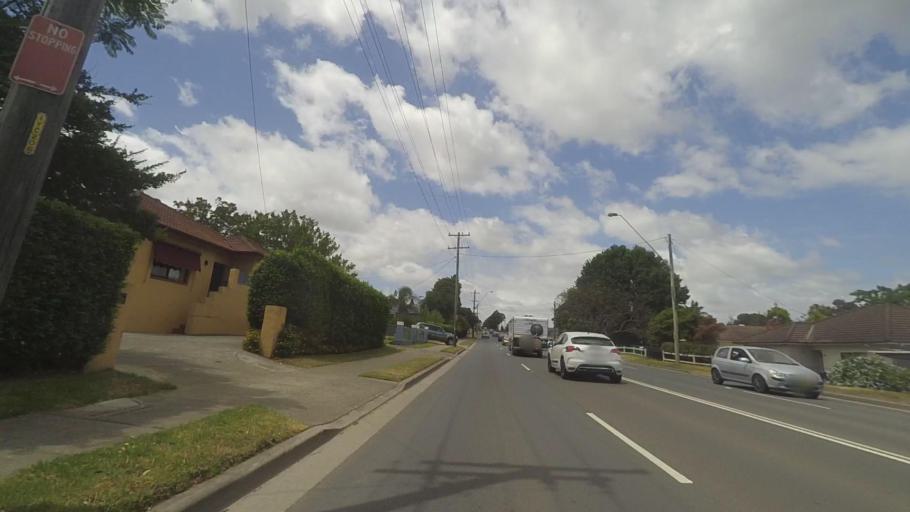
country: AU
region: New South Wales
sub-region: Shoalhaven Shire
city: Nowra
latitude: -34.8814
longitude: 150.6042
